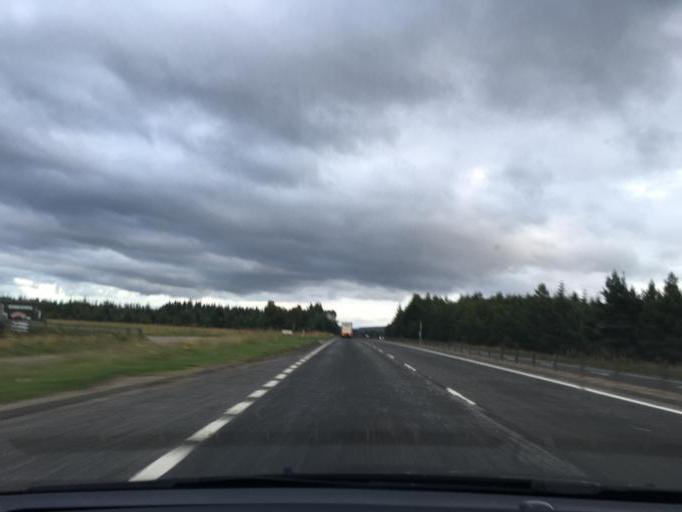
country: GB
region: Scotland
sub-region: Highland
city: Inverness
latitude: 57.4468
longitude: -4.1523
